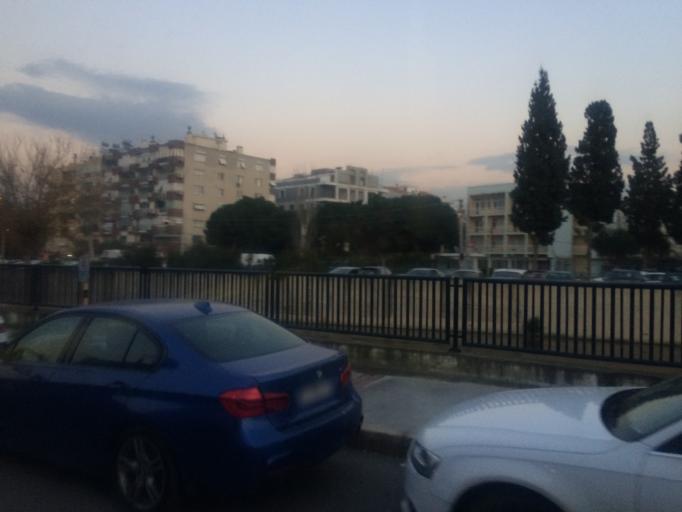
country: TR
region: Izmir
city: Karsiyaka
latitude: 38.4615
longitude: 27.0961
